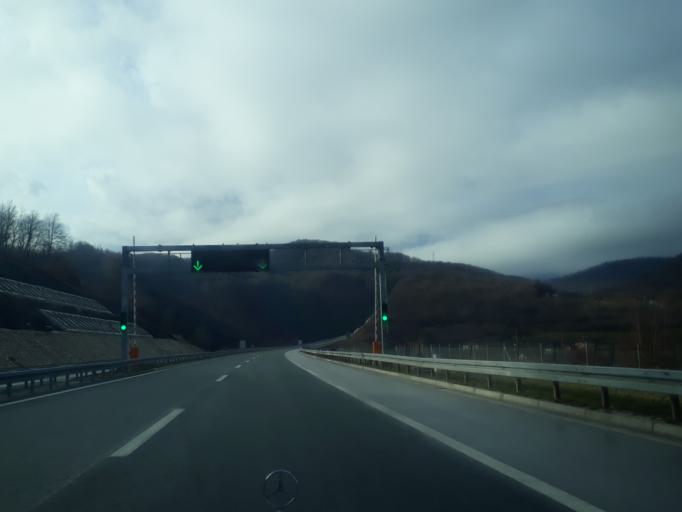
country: BA
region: Federation of Bosnia and Herzegovina
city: Polje
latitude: 43.8376
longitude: 18.1193
